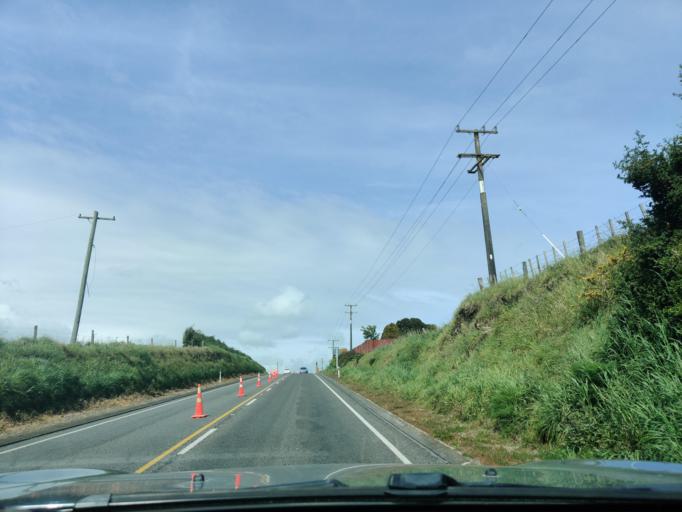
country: NZ
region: Taranaki
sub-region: South Taranaki District
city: Hawera
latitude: -39.6195
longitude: 174.3498
